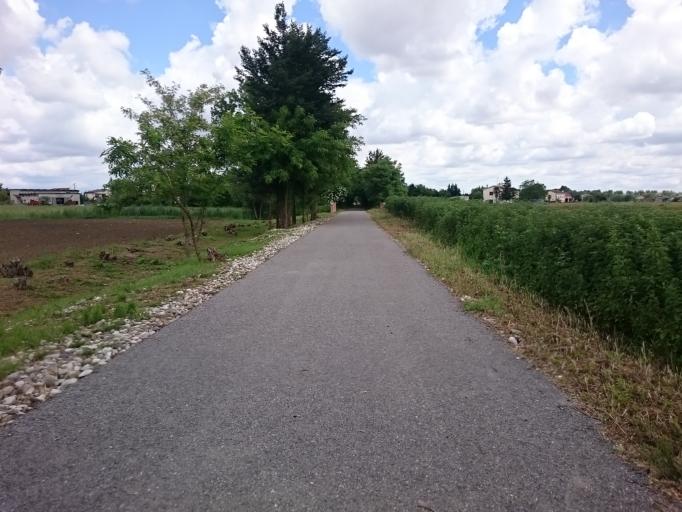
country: IT
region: Veneto
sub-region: Provincia di Padova
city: Campodoro
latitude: 45.5125
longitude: 11.7534
